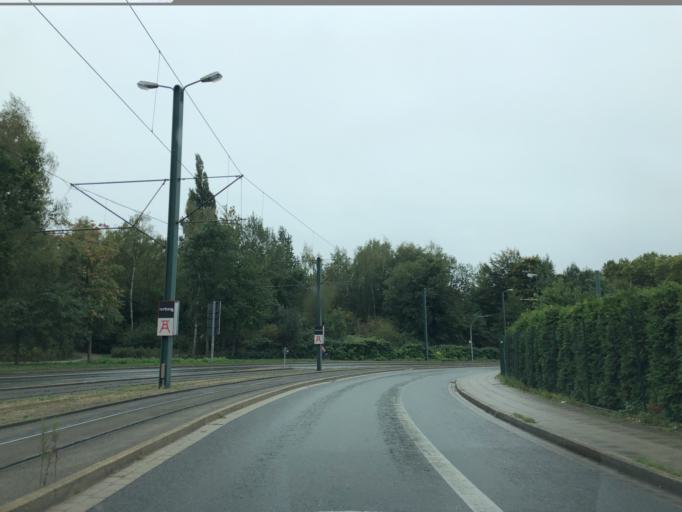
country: DE
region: North Rhine-Westphalia
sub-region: Regierungsbezirk Dusseldorf
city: Essen
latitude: 51.4828
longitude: 7.0437
